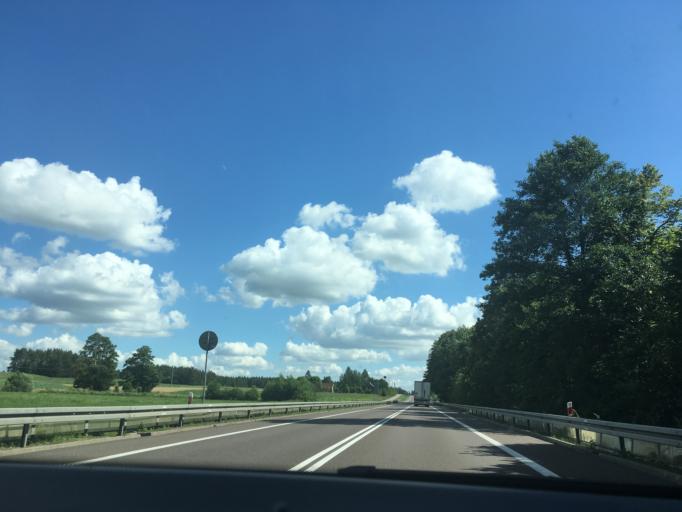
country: PL
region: Podlasie
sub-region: Powiat augustowski
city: Augustow
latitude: 53.7446
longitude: 23.0946
